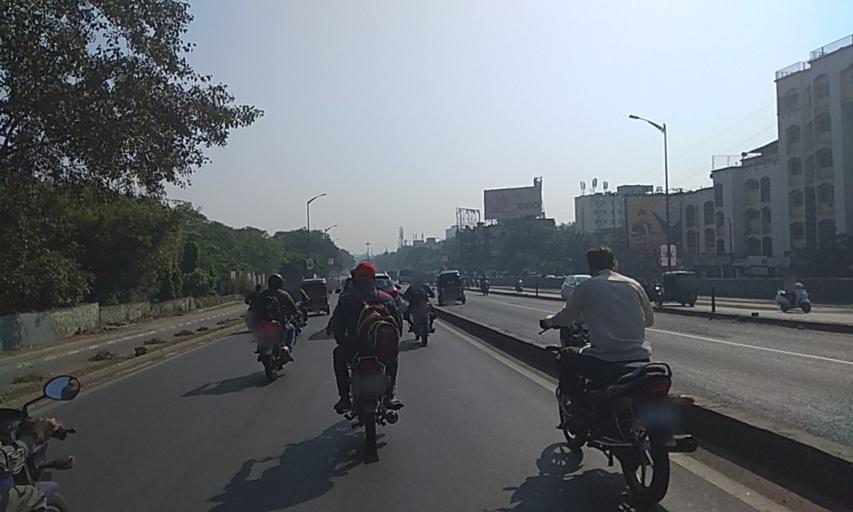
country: IN
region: Maharashtra
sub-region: Pune Division
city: Pune
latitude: 18.5049
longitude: 73.9185
